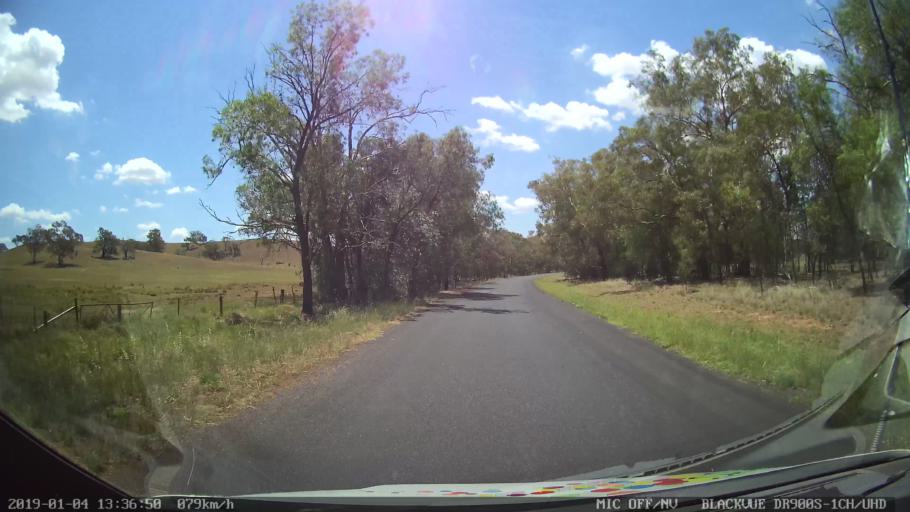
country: AU
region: New South Wales
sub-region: Dubbo Municipality
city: Dubbo
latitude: -32.5559
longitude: 148.5381
